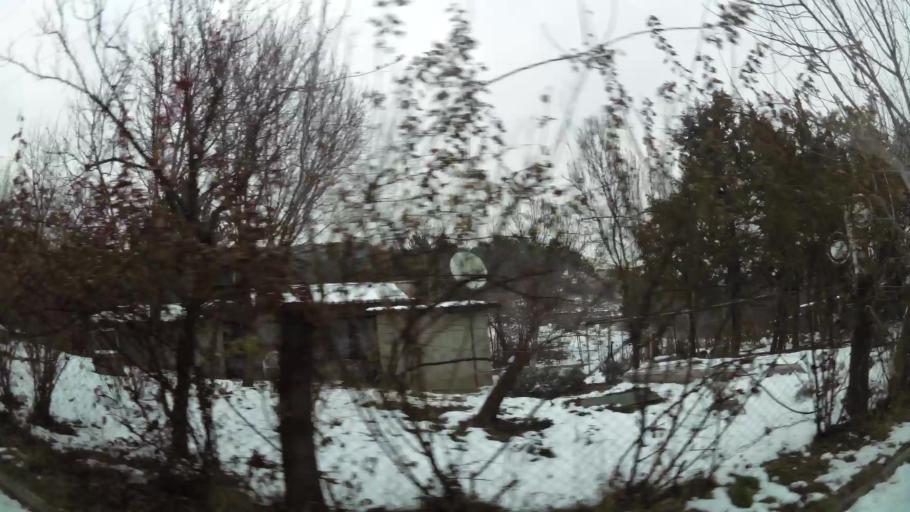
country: MK
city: Kondovo
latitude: 42.0522
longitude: 21.3419
